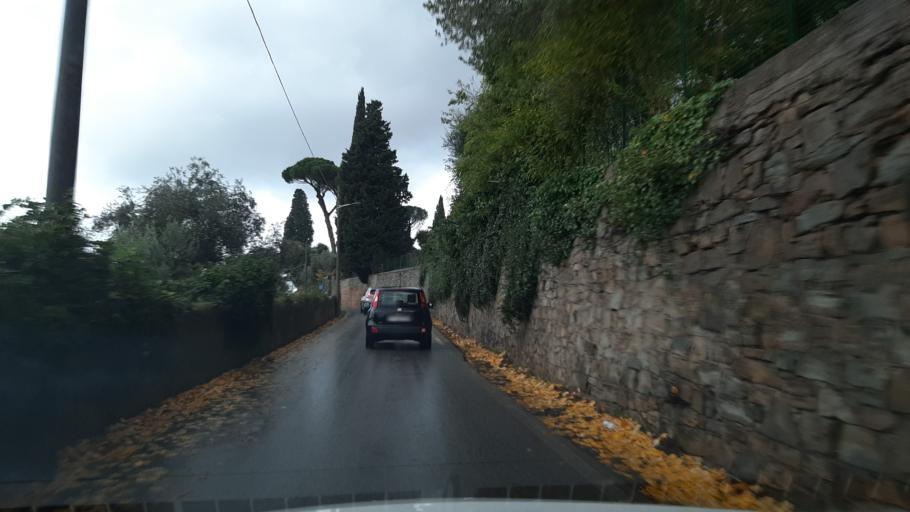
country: IT
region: Tuscany
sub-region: Province of Florence
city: Florence
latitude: 43.8112
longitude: 11.2552
